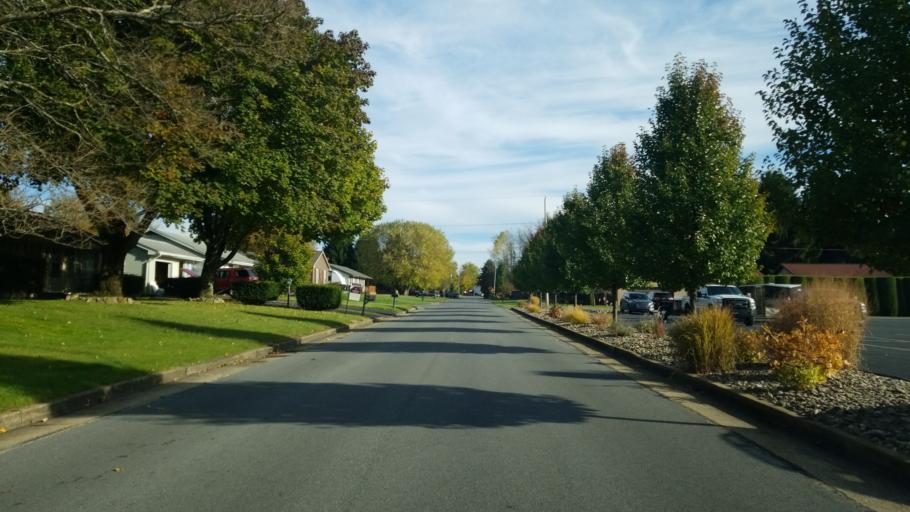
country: US
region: Pennsylvania
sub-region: Jefferson County
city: Brockway
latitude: 41.2506
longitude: -78.7891
